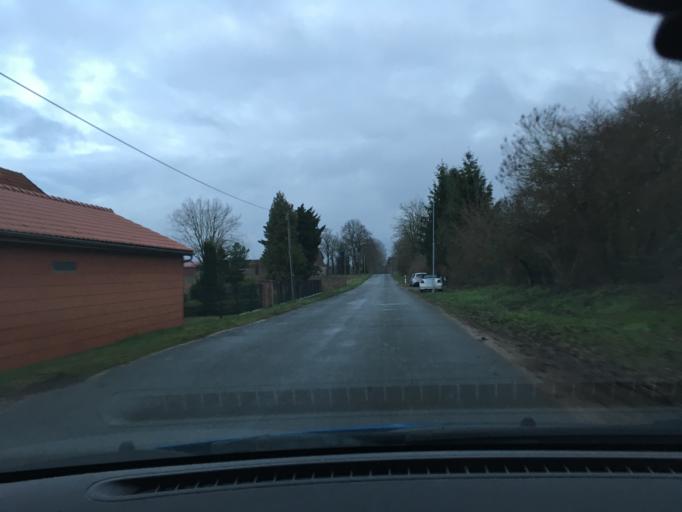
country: DE
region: Mecklenburg-Vorpommern
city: Nostorf
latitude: 53.3930
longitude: 10.6860
